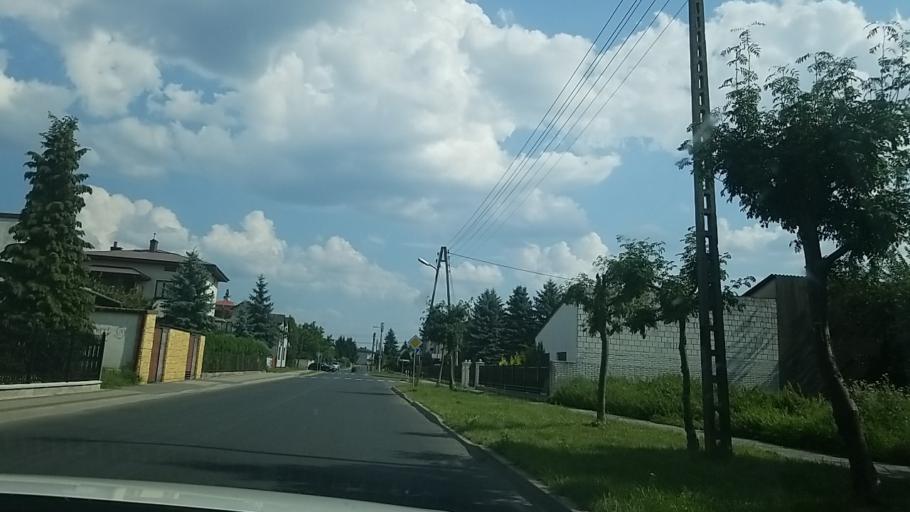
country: PL
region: Lublin Voivodeship
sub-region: Powiat janowski
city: Janow Lubelski
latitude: 50.7048
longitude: 22.4068
